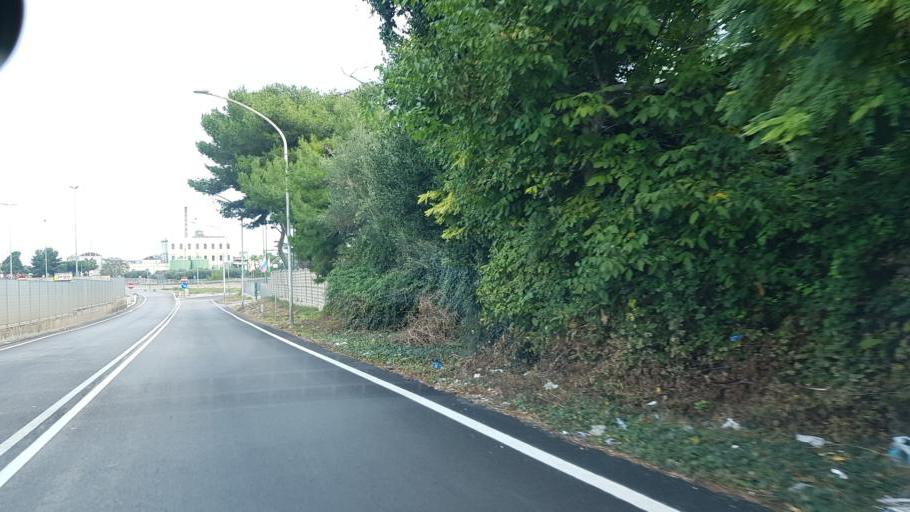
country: IT
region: Apulia
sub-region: Provincia di Bari
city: Bari
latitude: 41.0908
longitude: 16.8915
